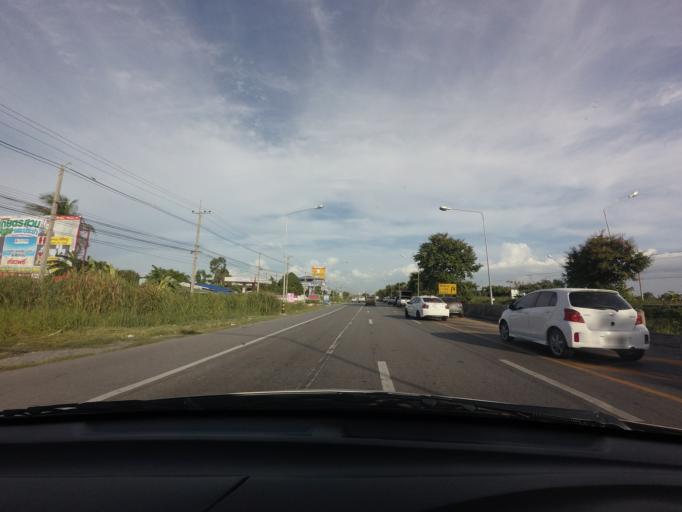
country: TH
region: Pathum Thani
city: Lat Lum Kaeo
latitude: 14.0191
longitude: 100.3602
